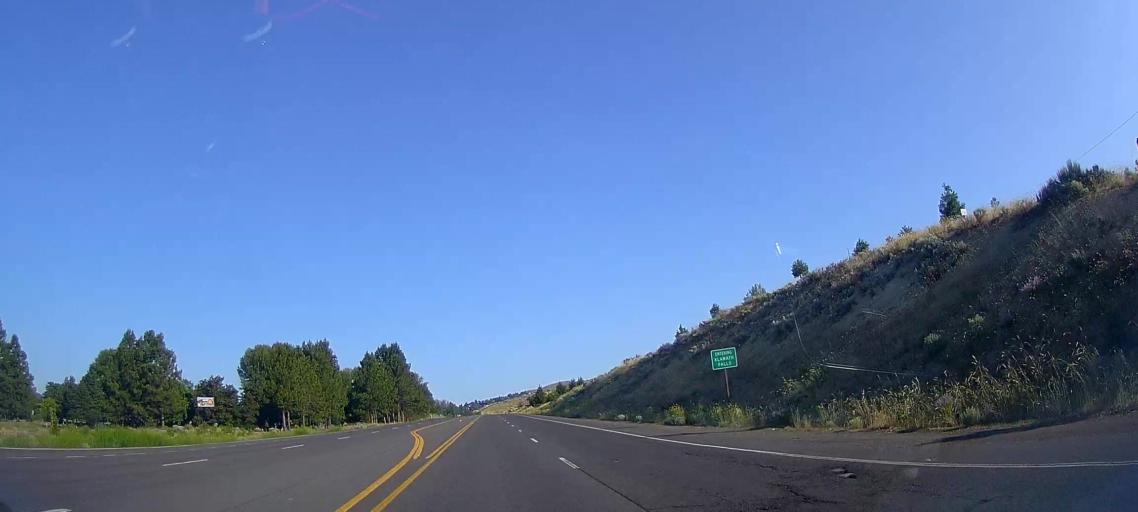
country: US
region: Oregon
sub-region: Klamath County
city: Altamont
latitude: 42.2180
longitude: -121.7480
